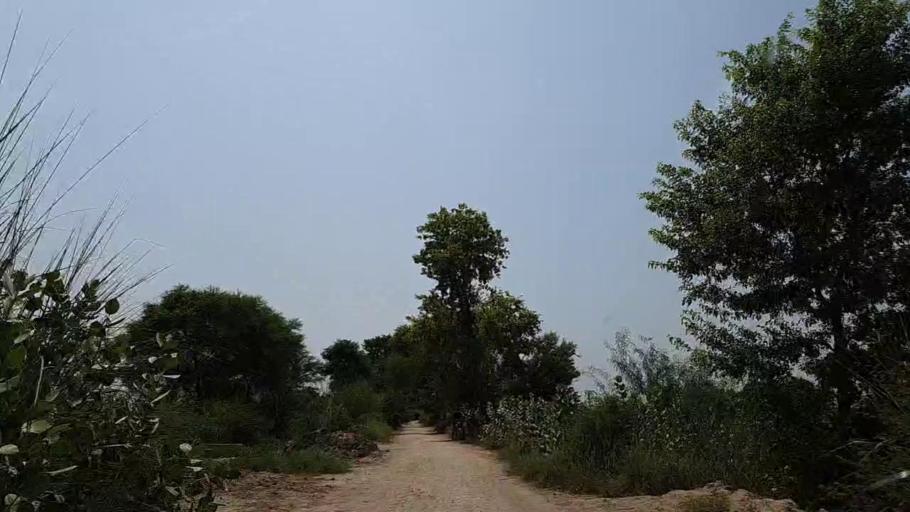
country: PK
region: Sindh
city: Adilpur
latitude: 27.9315
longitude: 69.3879
